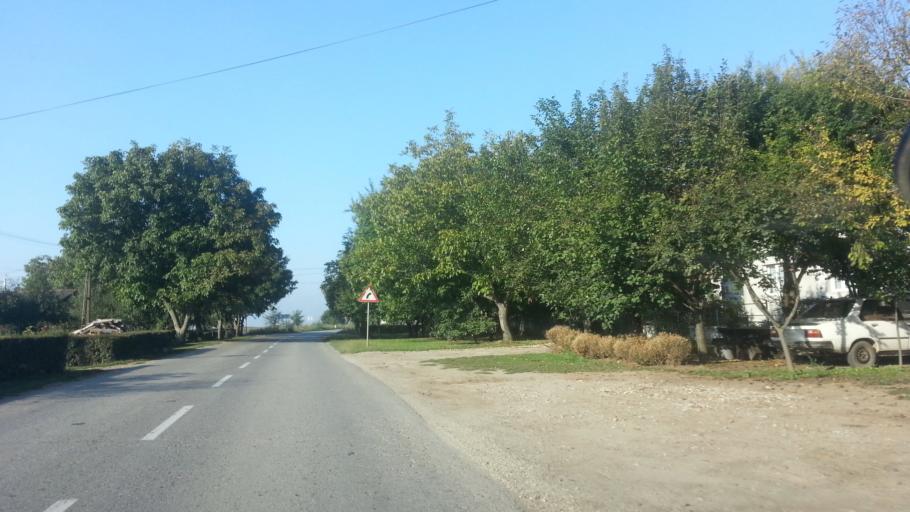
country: RS
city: Stari Banovci
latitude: 44.9779
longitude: 20.2717
